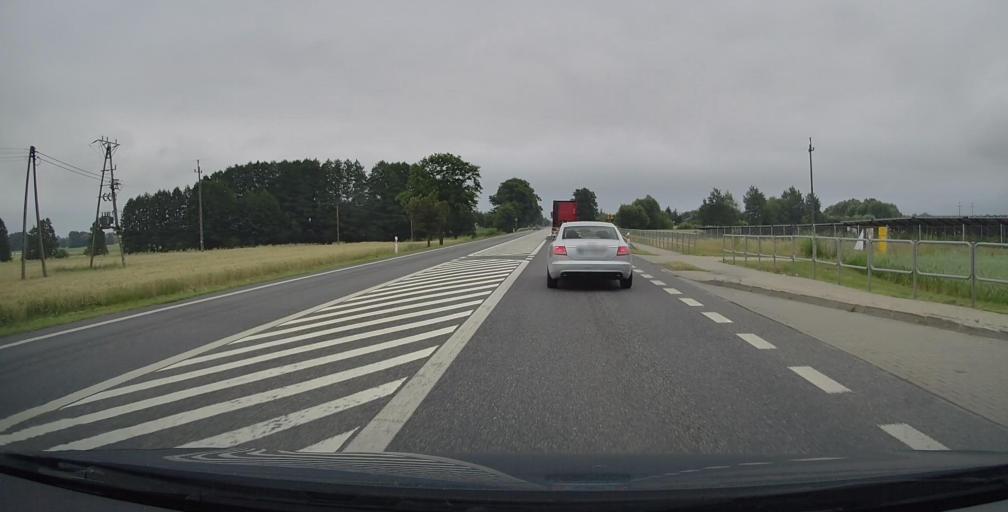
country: PL
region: Lublin Voivodeship
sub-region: Powiat bialski
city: Zalesie
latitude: 52.0351
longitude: 23.3371
